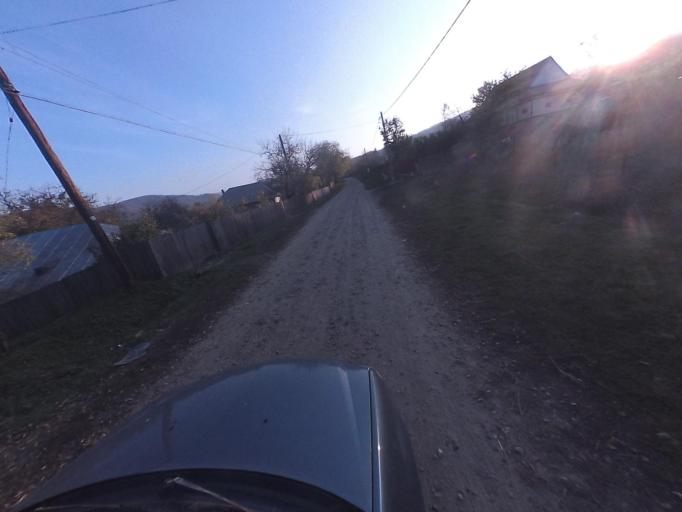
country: RO
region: Vaslui
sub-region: Comuna Bacesti
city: Bacesti
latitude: 46.8030
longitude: 27.2248
